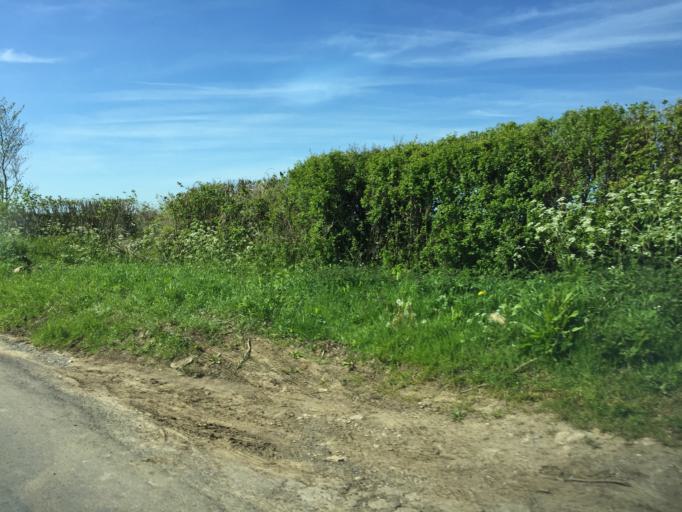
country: GB
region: England
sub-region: Wiltshire
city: Luckington
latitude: 51.5608
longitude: -2.2441
